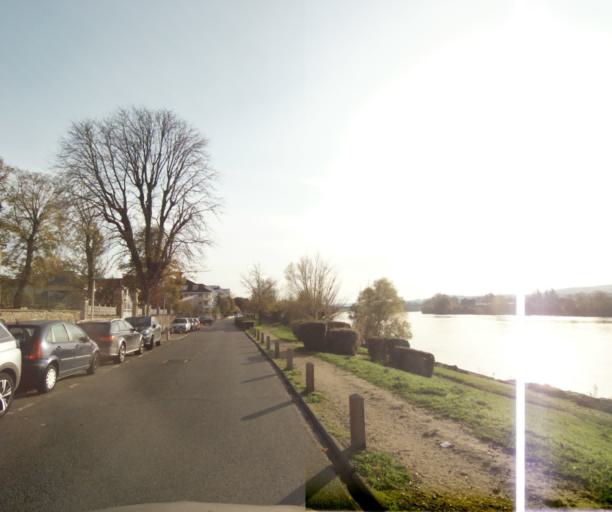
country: FR
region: Ile-de-France
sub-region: Departement des Yvelines
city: Triel-sur-Seine
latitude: 48.9777
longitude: 2.0029
